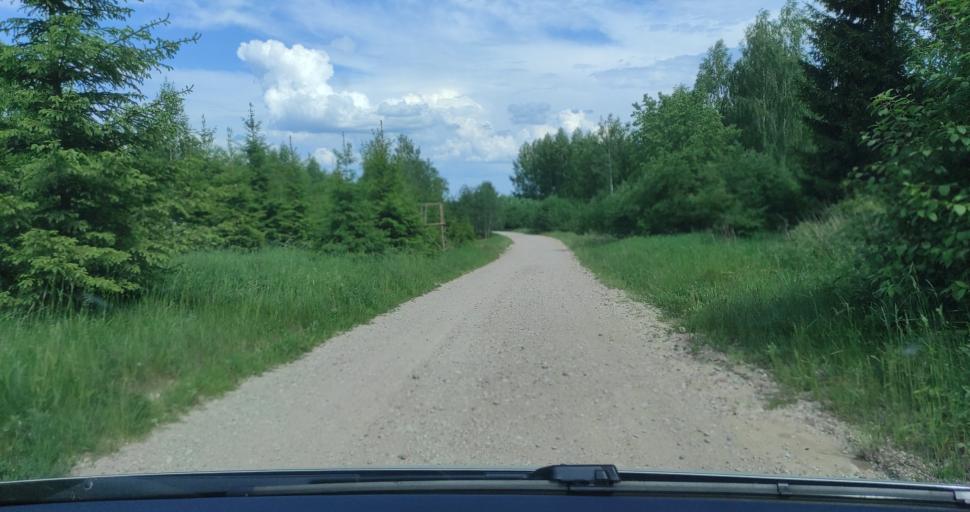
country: LV
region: Kuldigas Rajons
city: Kuldiga
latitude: 56.8603
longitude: 21.9288
